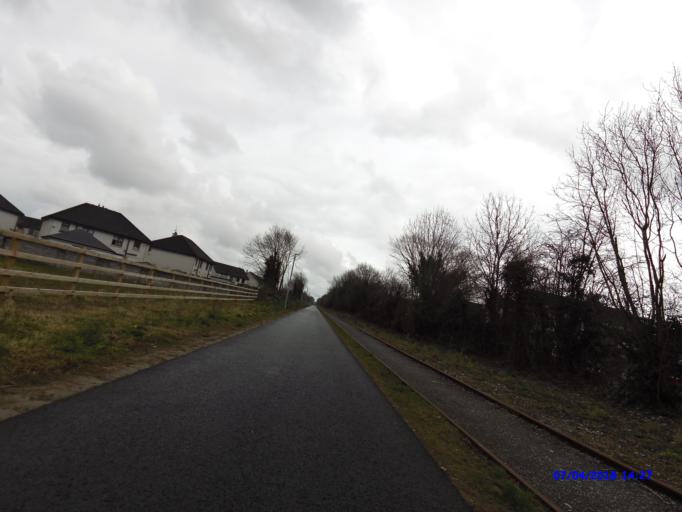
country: IE
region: Leinster
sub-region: An Iarmhi
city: Athlone
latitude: 53.4255
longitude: -7.9174
